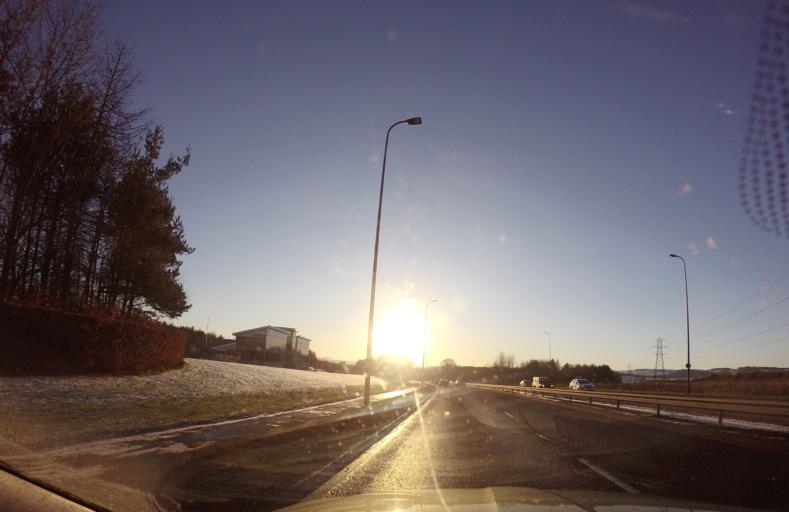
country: GB
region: Scotland
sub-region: Angus
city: Muirhead
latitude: 56.4715
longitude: -3.0560
